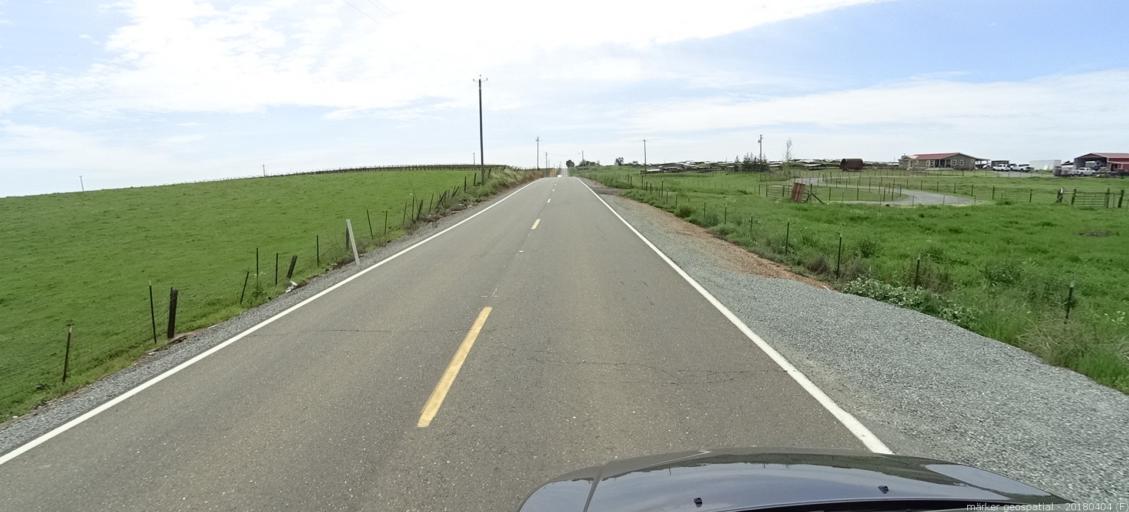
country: US
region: California
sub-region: Sacramento County
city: Clay
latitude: 38.2875
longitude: -121.1713
